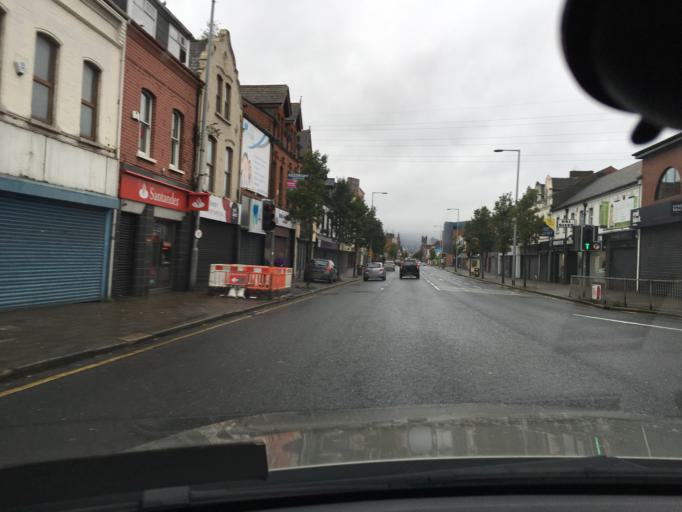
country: GB
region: Northern Ireland
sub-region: Castlereagh District
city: Castlereagh
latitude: 54.5976
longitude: -5.8885
